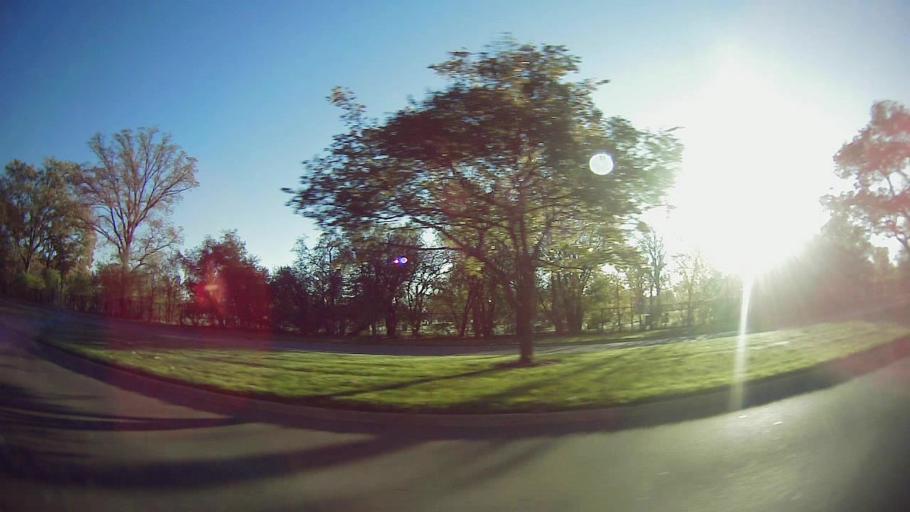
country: US
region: Michigan
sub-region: Oakland County
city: Berkley
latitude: 42.5060
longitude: -83.1841
